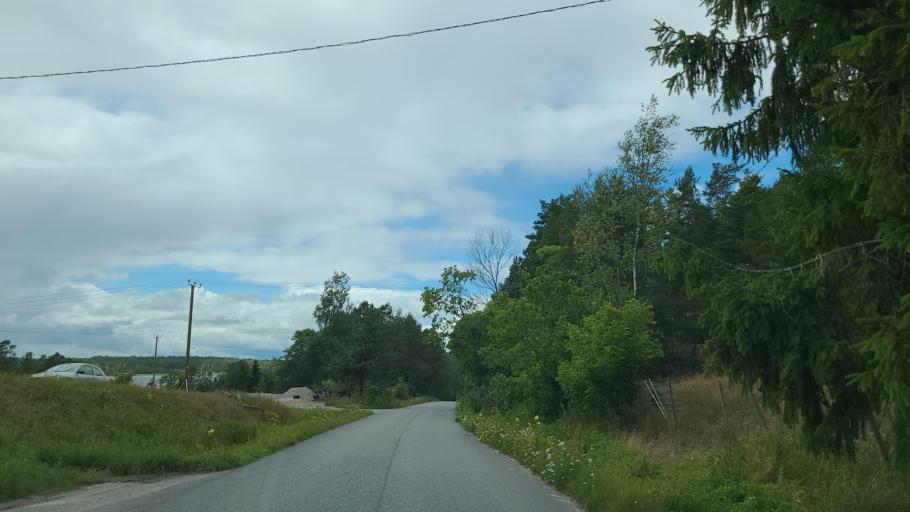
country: FI
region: Varsinais-Suomi
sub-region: Aboland-Turunmaa
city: Nagu
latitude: 60.1639
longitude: 22.0039
